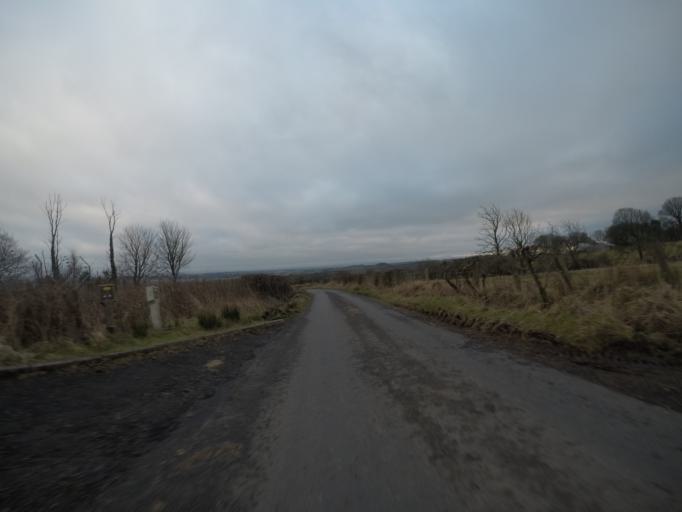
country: GB
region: Scotland
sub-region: North Ayrshire
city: Dalry
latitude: 55.7173
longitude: -4.7563
